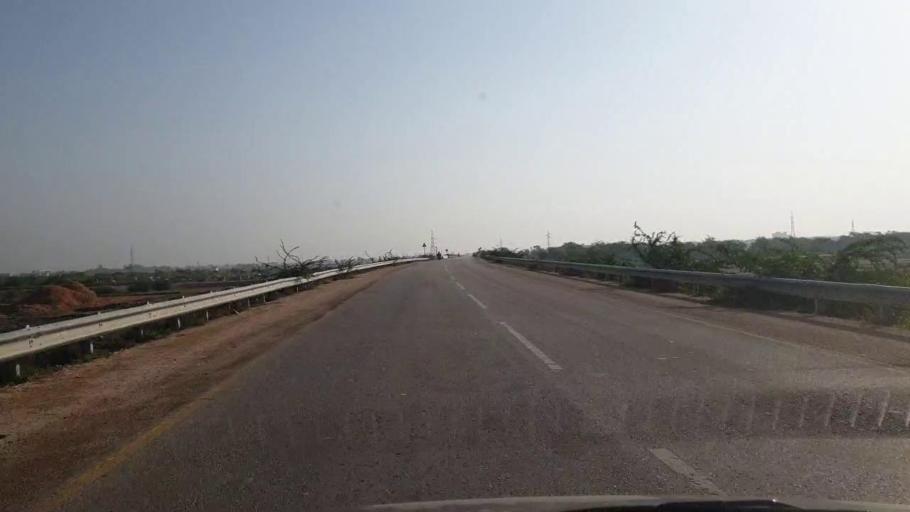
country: PK
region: Sindh
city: Badin
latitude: 24.6781
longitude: 68.8152
